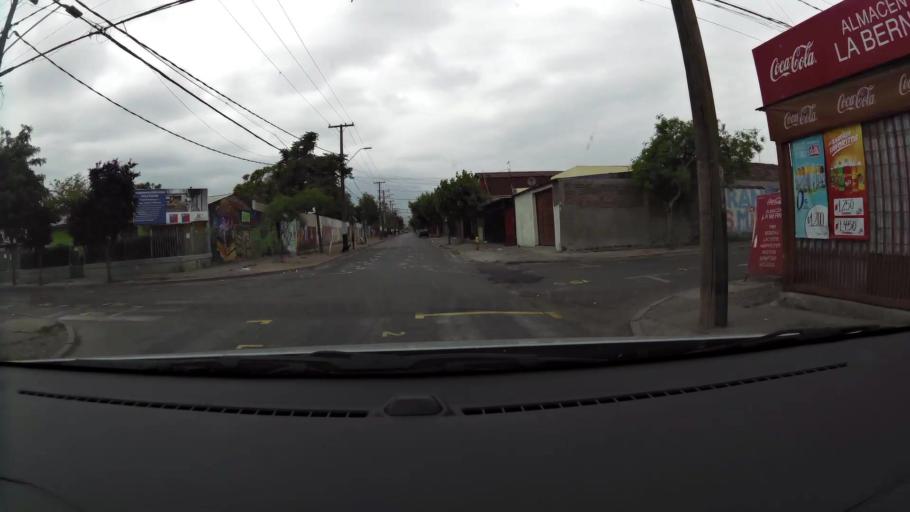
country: CL
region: Santiago Metropolitan
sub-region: Provincia de Santiago
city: Santiago
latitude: -33.5125
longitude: -70.6898
